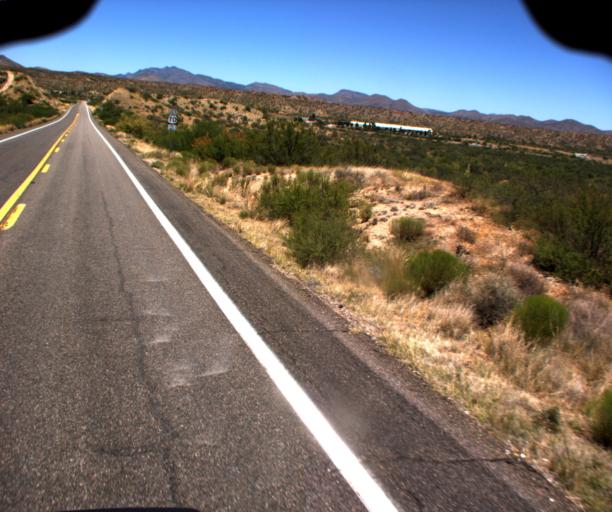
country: US
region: Arizona
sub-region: Gila County
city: Globe
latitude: 33.3649
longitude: -110.7368
